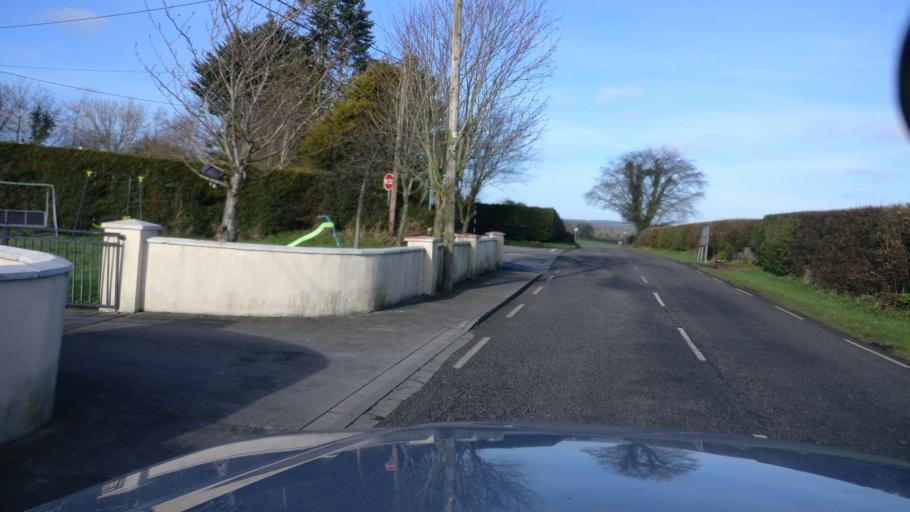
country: IE
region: Leinster
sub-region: Kilkenny
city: Castlecomer
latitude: 52.8708
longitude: -7.1643
